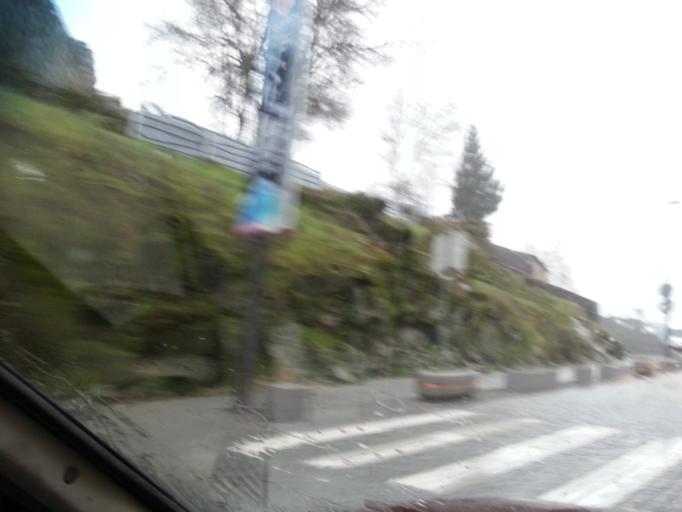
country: PT
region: Guarda
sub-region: Guarda
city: Guarda
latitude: 40.5405
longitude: -7.2667
